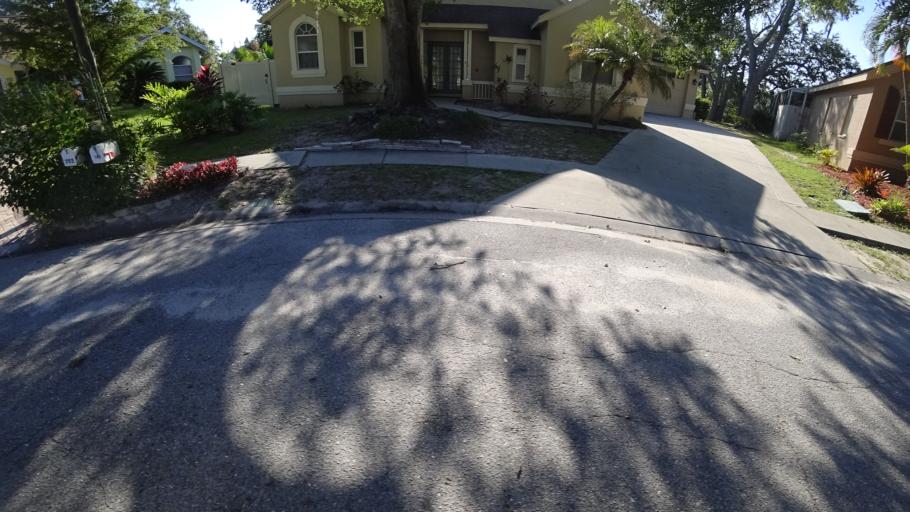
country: US
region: Florida
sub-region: Manatee County
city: Ellenton
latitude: 27.5014
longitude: -82.5046
